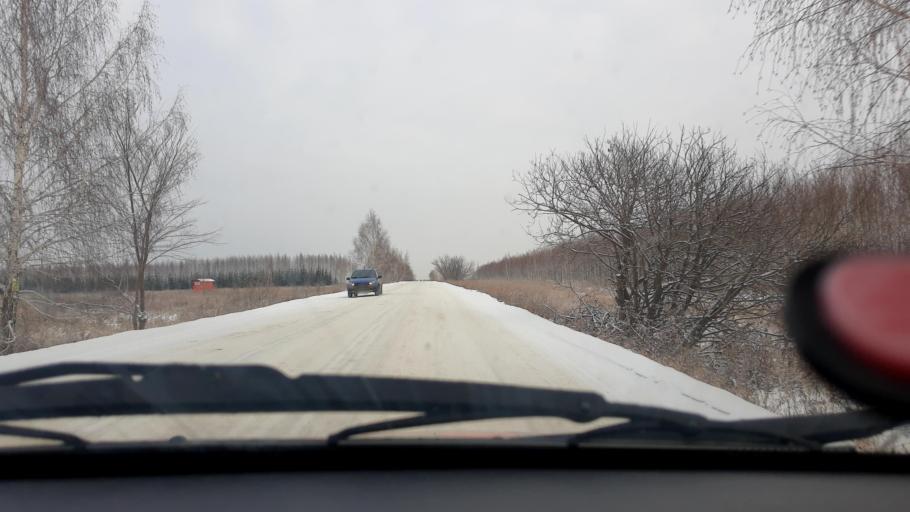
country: RU
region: Bashkortostan
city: Iglino
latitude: 54.7486
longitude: 56.2820
